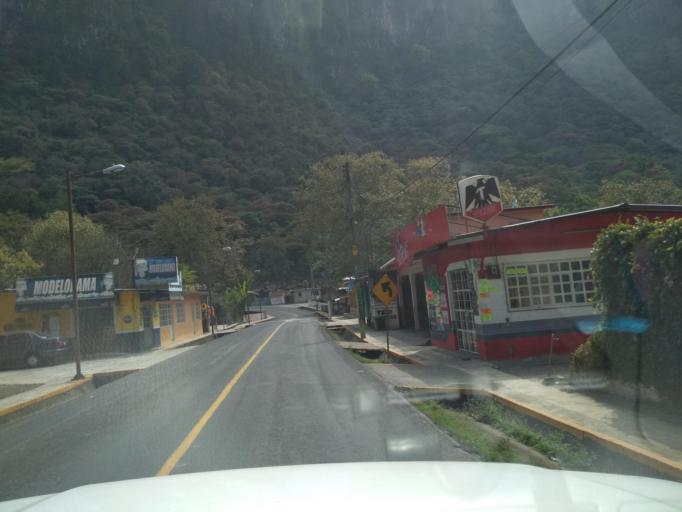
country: MX
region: Veracruz
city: Jalapilla
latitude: 18.7896
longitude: -97.0947
